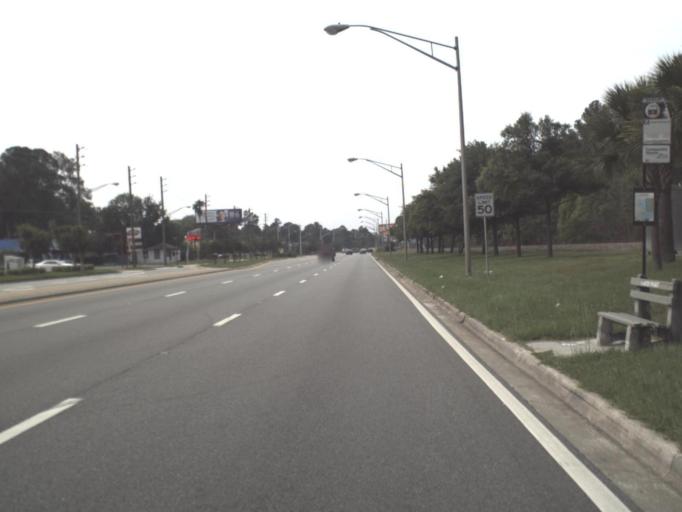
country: US
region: Florida
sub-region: Clay County
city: Orange Park
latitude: 30.2456
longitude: -81.6974
